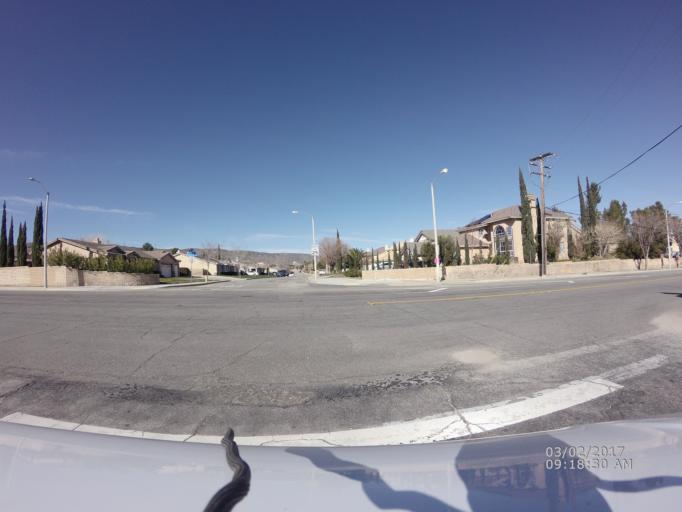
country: US
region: California
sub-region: Los Angeles County
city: Quartz Hill
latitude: 34.6345
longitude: -118.2187
